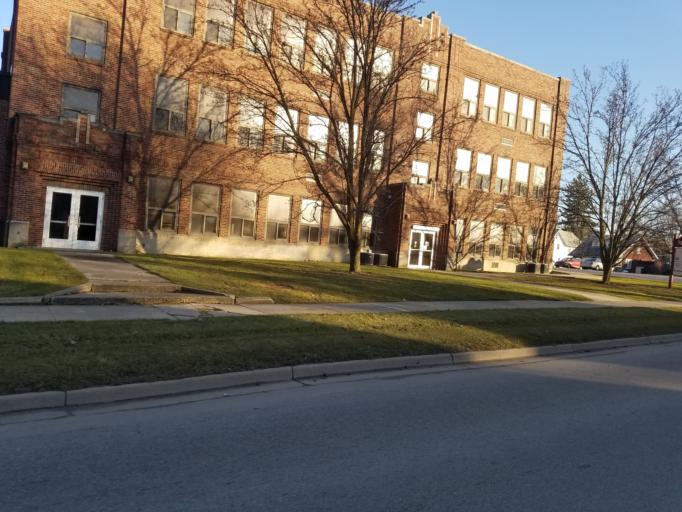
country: US
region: Indiana
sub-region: Elkhart County
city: Nappanee
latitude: 41.4473
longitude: -86.0014
